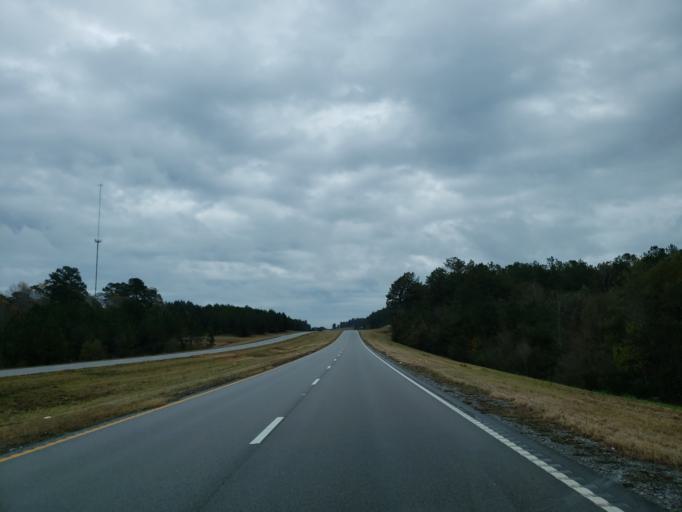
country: US
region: Mississippi
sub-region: Wayne County
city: Waynesboro
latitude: 31.6895
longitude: -88.7093
